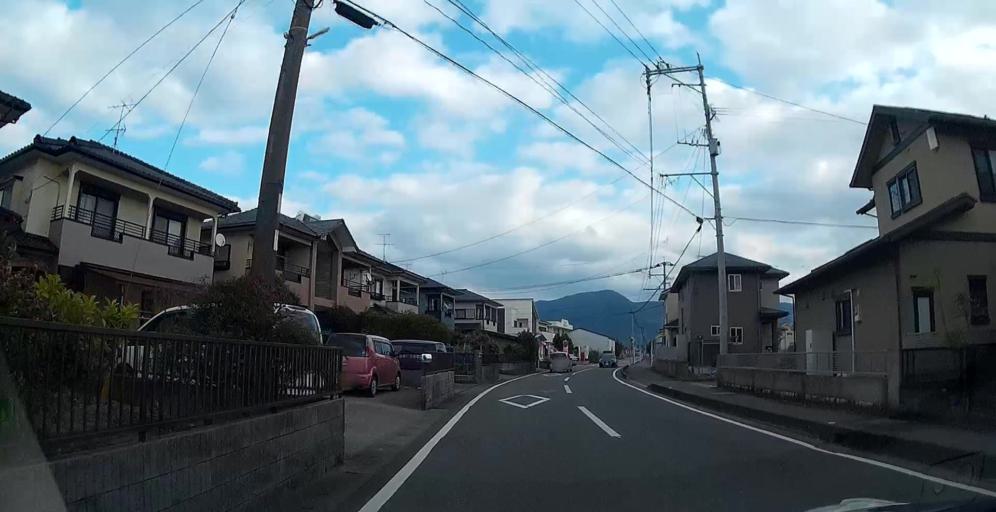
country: JP
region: Kumamoto
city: Yatsushiro
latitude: 32.5384
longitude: 130.6284
